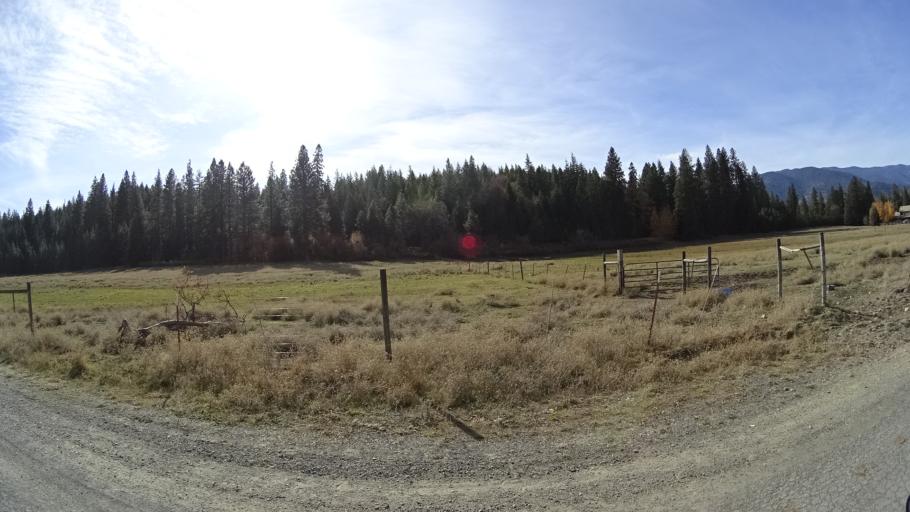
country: US
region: California
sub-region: Siskiyou County
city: Weed
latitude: 41.4328
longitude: -122.4076
